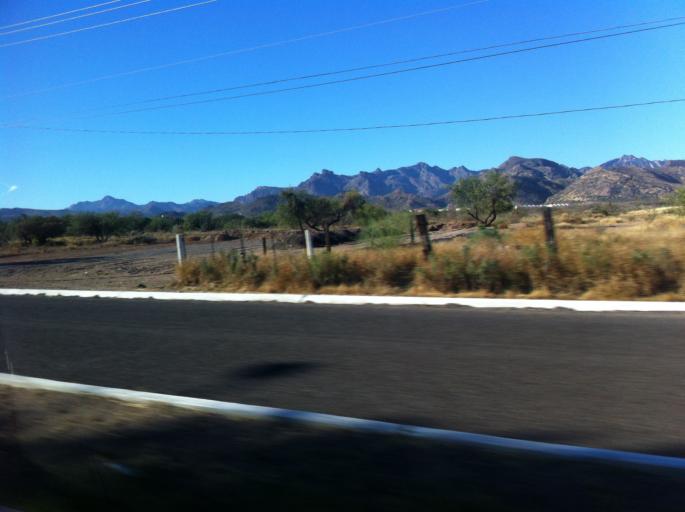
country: MX
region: Sonora
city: Heroica Guaymas
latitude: 27.9685
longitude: -111.0066
